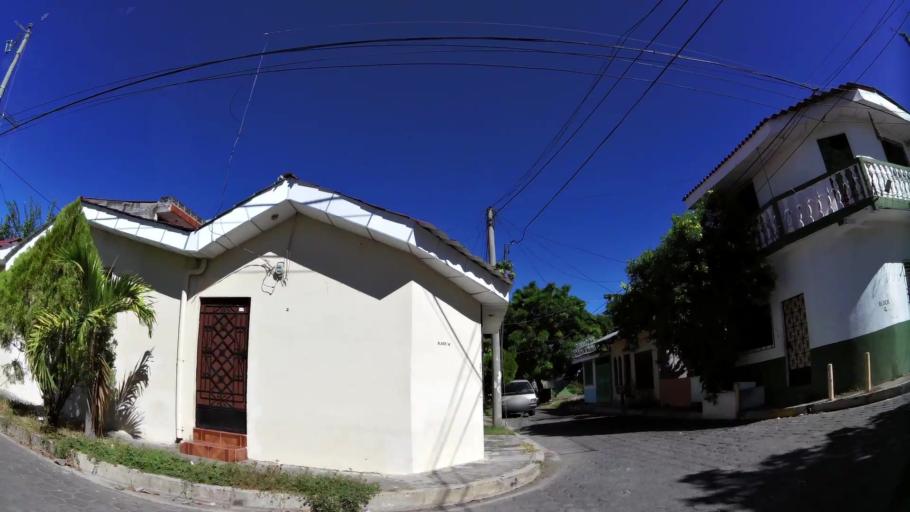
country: SV
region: San Miguel
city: San Miguel
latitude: 13.4634
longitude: -88.1599
